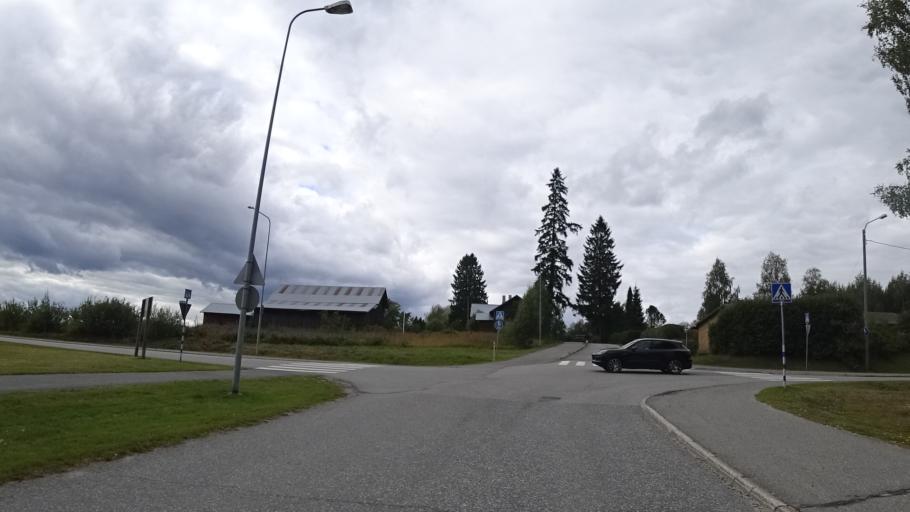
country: FI
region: North Karelia
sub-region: Joensuu
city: Ilomantsi
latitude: 62.6674
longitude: 30.9287
